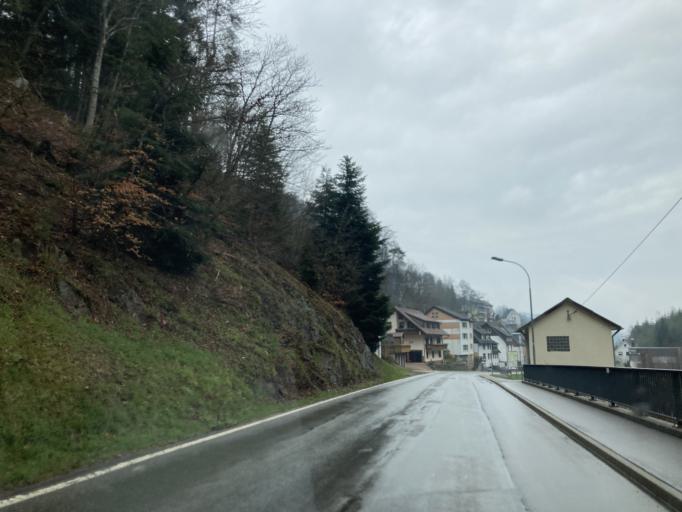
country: DE
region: Baden-Wuerttemberg
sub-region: Freiburg Region
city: Lauterbach/Schwarzwald
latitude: 48.2286
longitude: 8.3335
